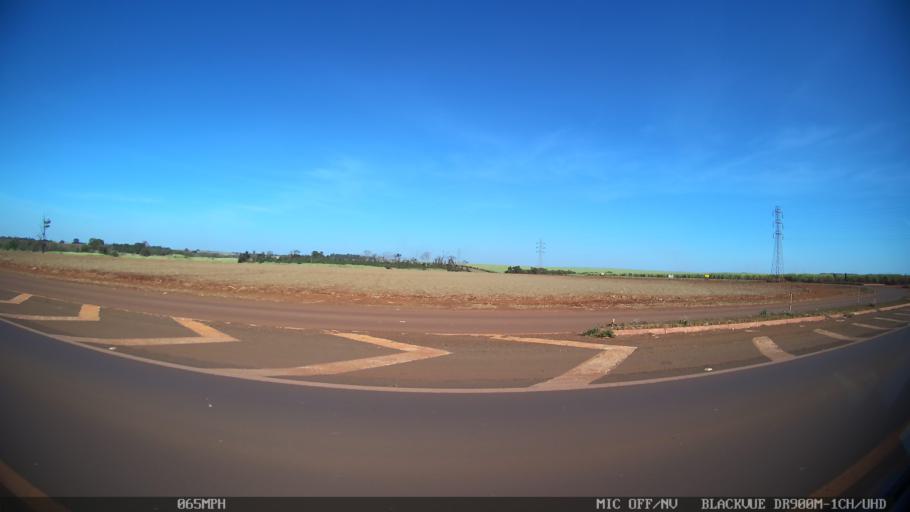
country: BR
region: Sao Paulo
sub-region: Guaira
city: Guaira
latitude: -20.4459
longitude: -48.4156
